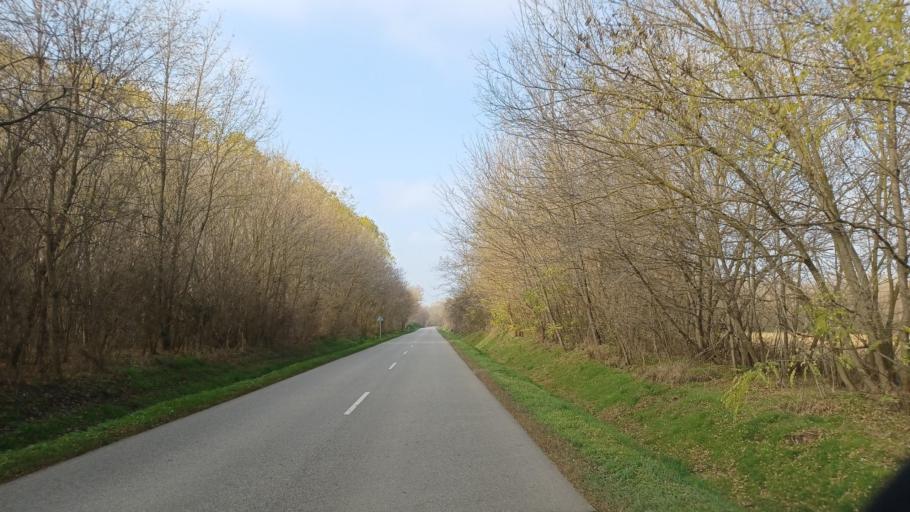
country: HU
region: Tolna
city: Tengelic
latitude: 46.5513
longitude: 18.7355
